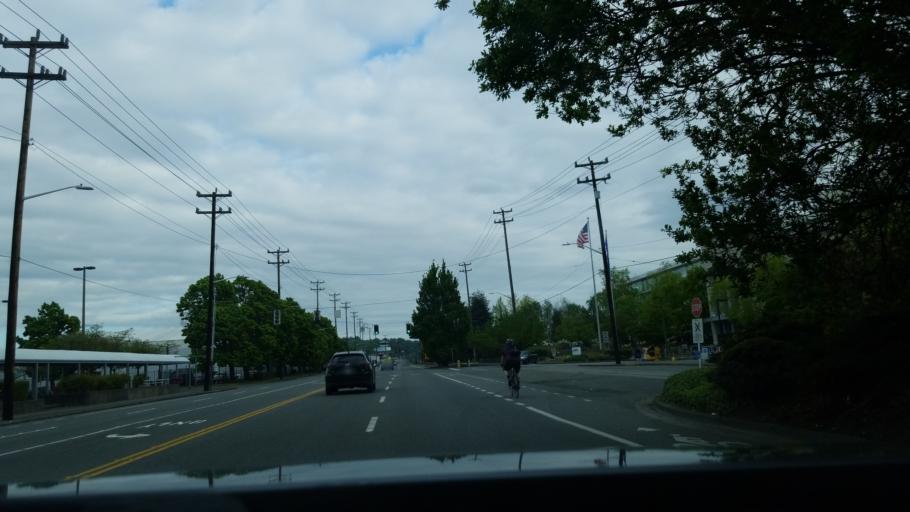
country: US
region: Washington
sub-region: King County
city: Boulevard Park
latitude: 47.5336
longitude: -122.3121
